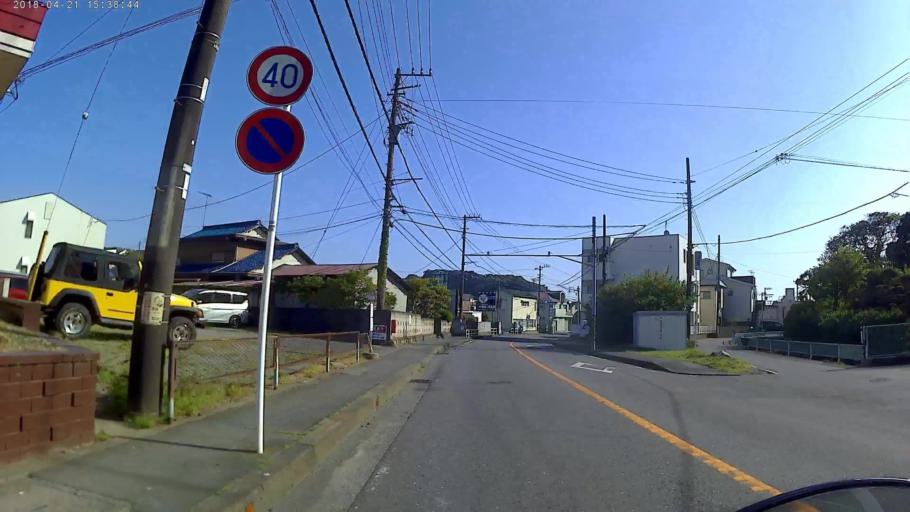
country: JP
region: Kanagawa
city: Fujisawa
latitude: 35.3169
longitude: 139.5031
